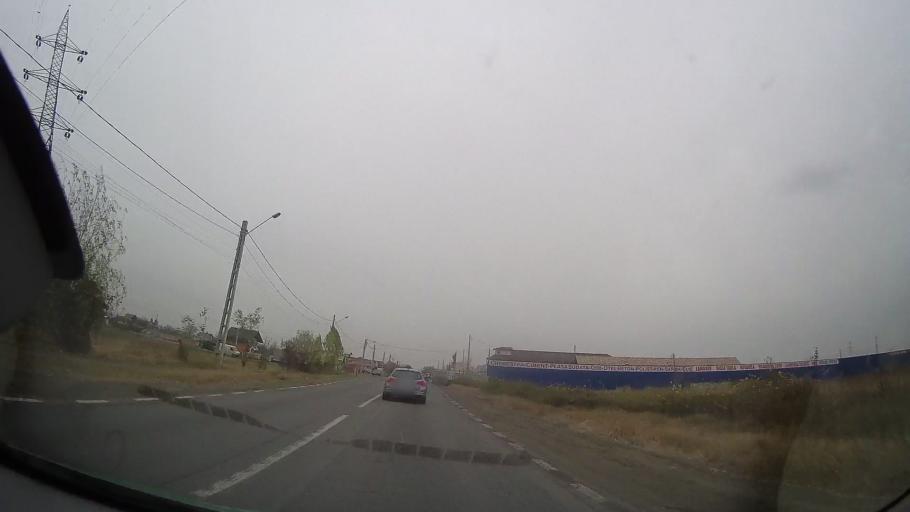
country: RO
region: Prahova
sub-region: Comuna Blejoiu
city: Ploiestiori
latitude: 44.9739
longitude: 26.0192
